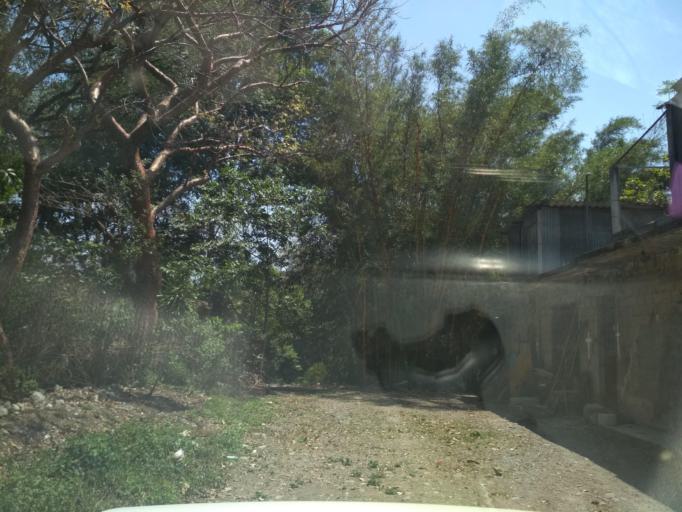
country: MX
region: Veracruz
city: Rio Blanco
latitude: 18.8324
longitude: -97.1107
